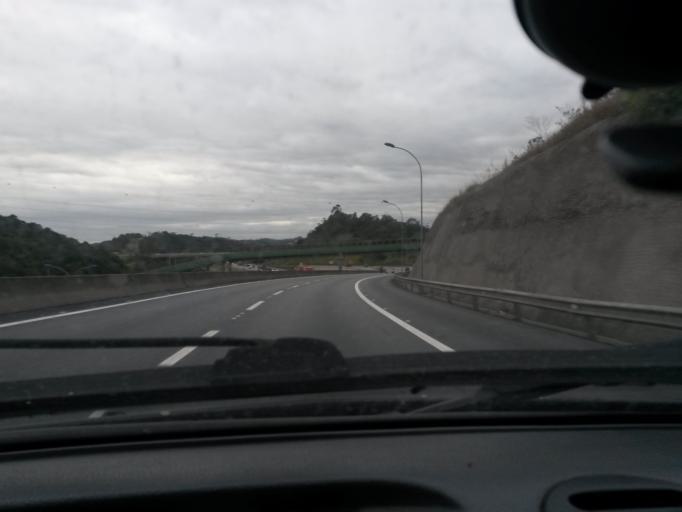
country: BR
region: Sao Paulo
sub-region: Sao Bernardo Do Campo
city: Sao Bernardo do Campo
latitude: -23.7552
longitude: -46.5344
